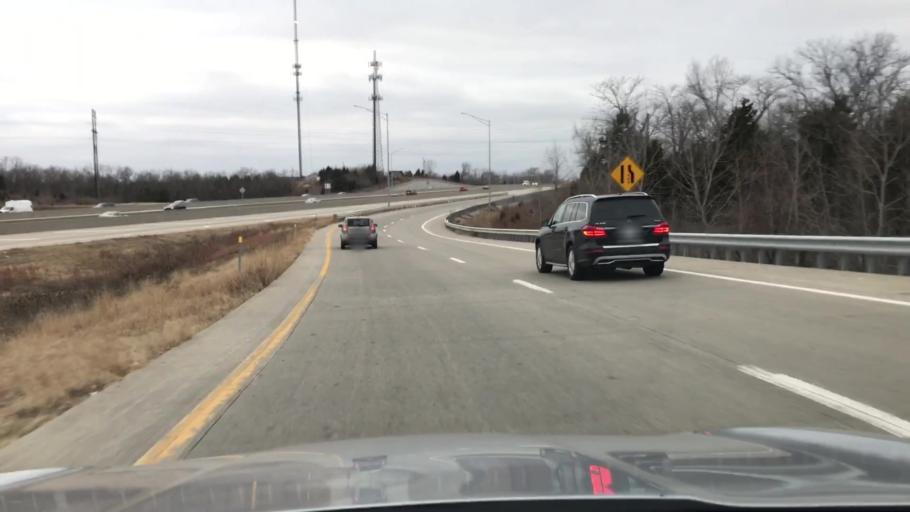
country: US
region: Missouri
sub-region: Jackson County
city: Lees Summit
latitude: 38.9347
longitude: -94.4131
